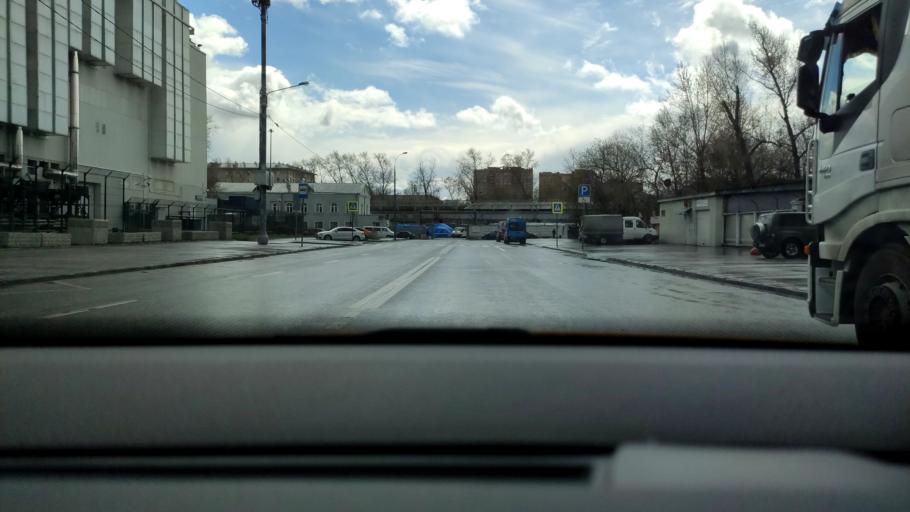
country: RU
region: Moscow
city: Lefortovo
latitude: 55.7367
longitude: 37.7203
